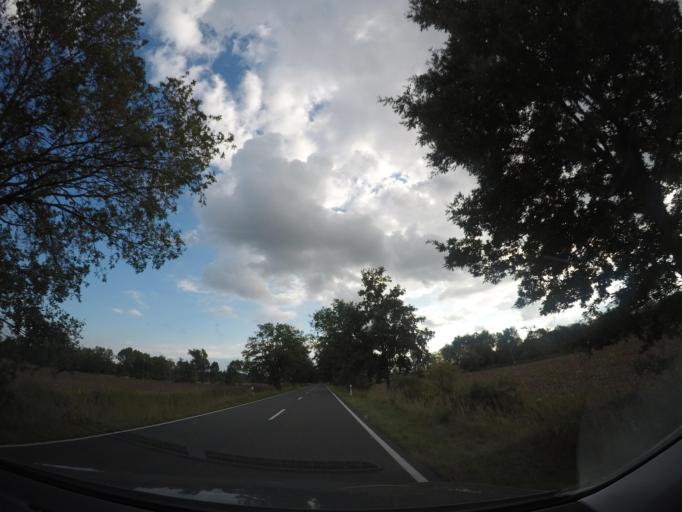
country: DE
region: Saxony-Anhalt
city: Mieste
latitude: 52.4460
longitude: 11.1466
